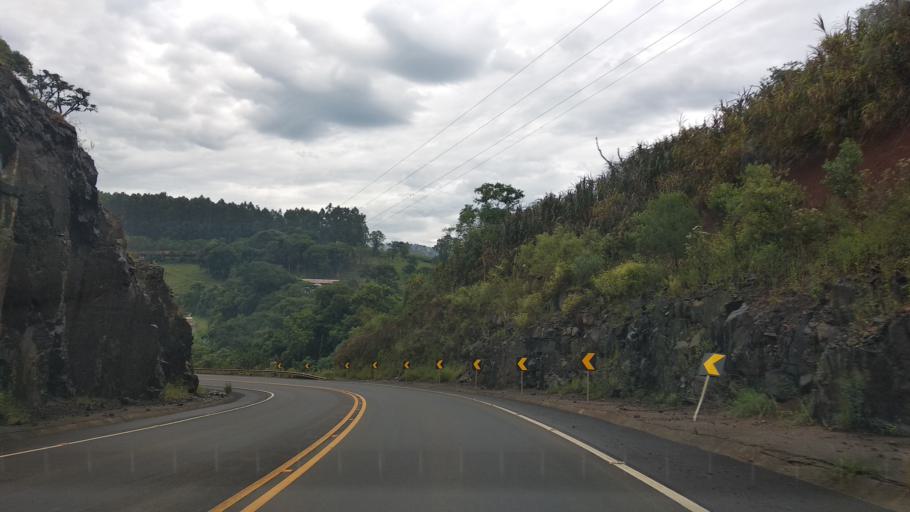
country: BR
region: Santa Catarina
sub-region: Videira
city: Videira
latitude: -27.0628
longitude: -51.2366
